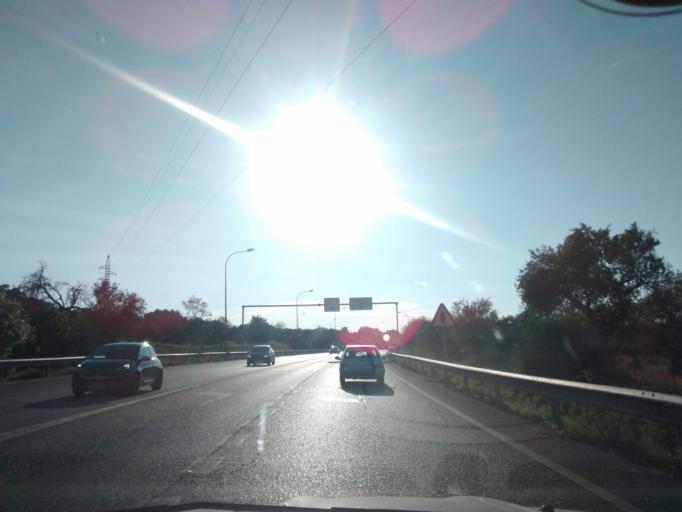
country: ES
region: Balearic Islands
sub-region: Illes Balears
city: Alcudia
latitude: 39.8421
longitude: 3.1007
